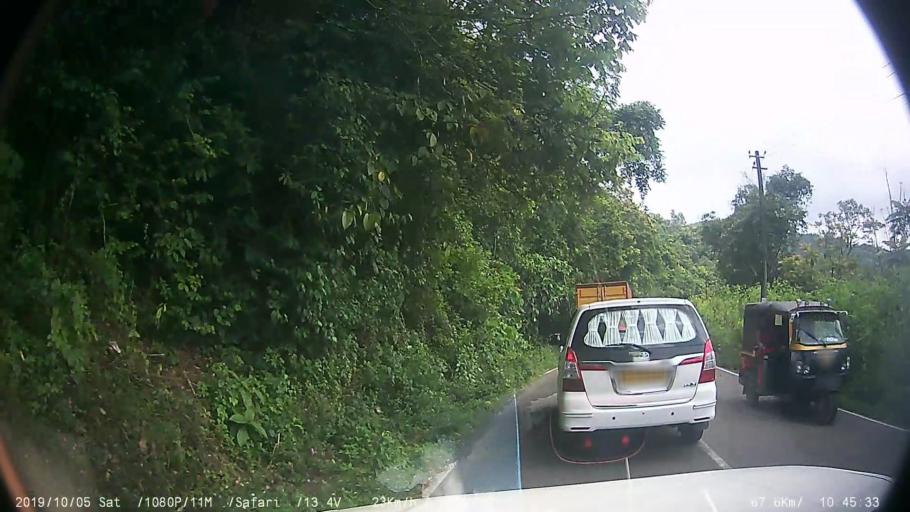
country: IN
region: Kerala
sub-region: Kottayam
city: Erattupetta
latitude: 9.5578
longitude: 76.9747
